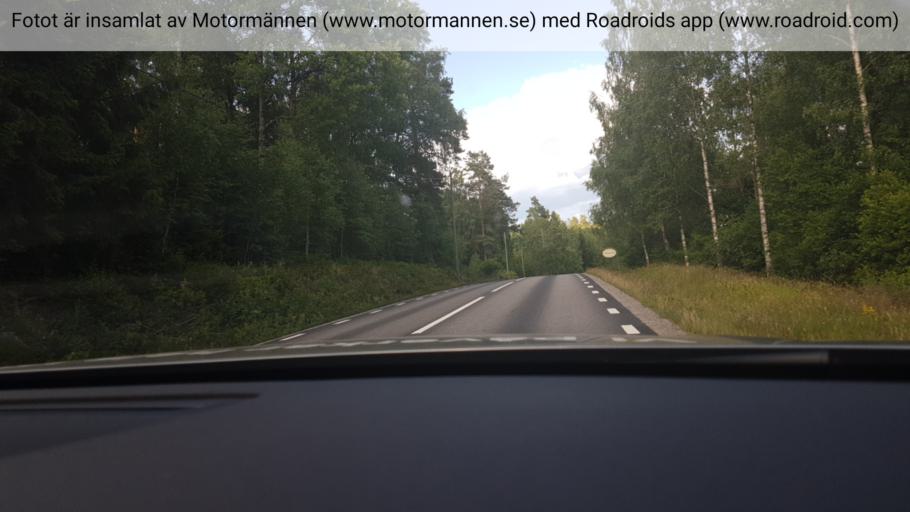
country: SE
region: Vaestra Goetaland
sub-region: Svenljunga Kommun
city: Svenljunga
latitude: 57.4646
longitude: 13.1923
